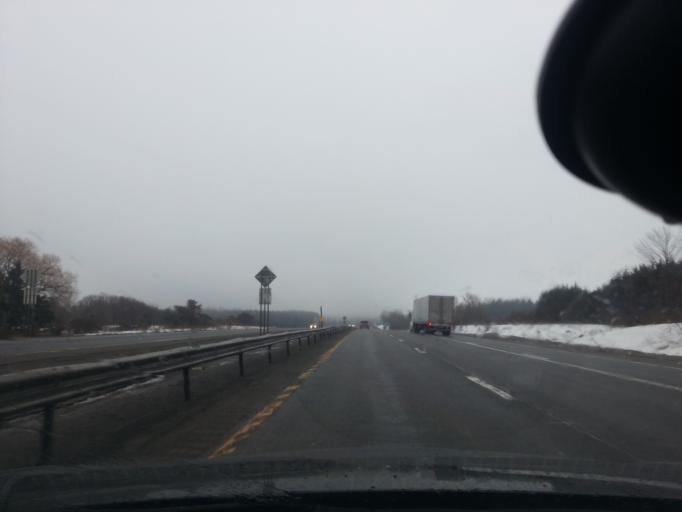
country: US
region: New York
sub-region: Onondaga County
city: Nedrow
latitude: 42.8812
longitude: -76.1101
